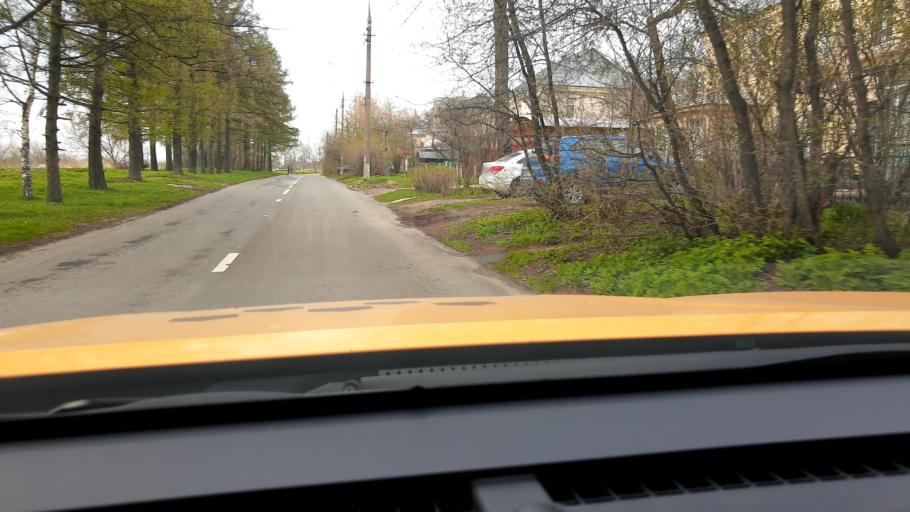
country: RU
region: Moscow
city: Severnyy
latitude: 55.9388
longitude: 37.5470
